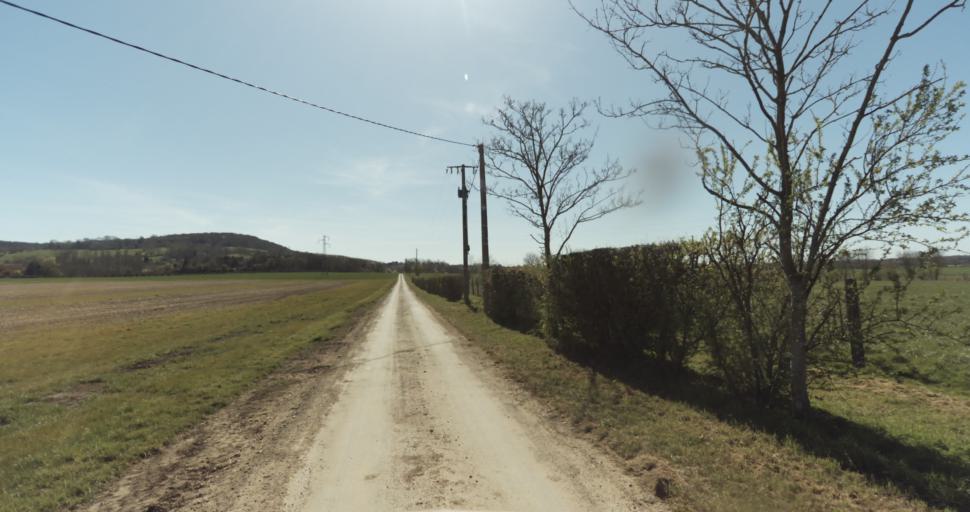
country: FR
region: Lower Normandy
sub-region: Departement du Calvados
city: Saint-Pierre-sur-Dives
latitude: 49.0230
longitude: 0.0315
